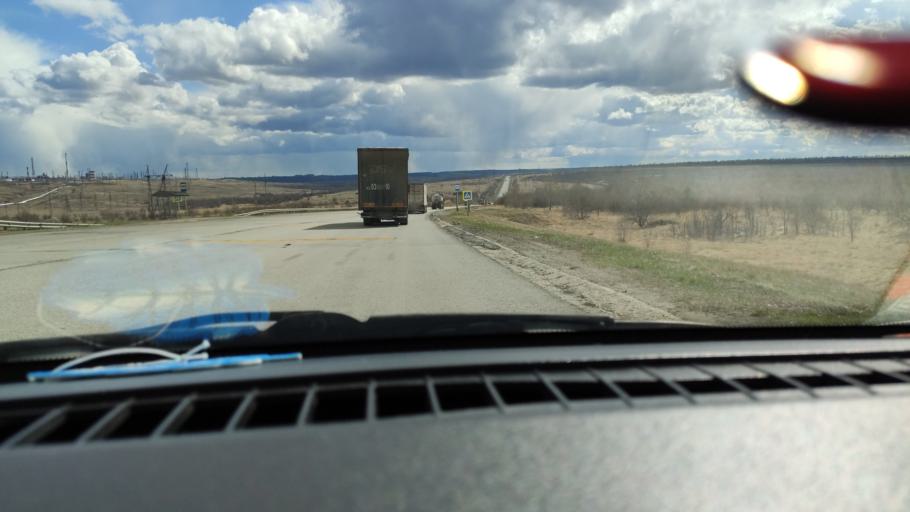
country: RU
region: Samara
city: Varlamovo
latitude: 53.1022
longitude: 48.3566
